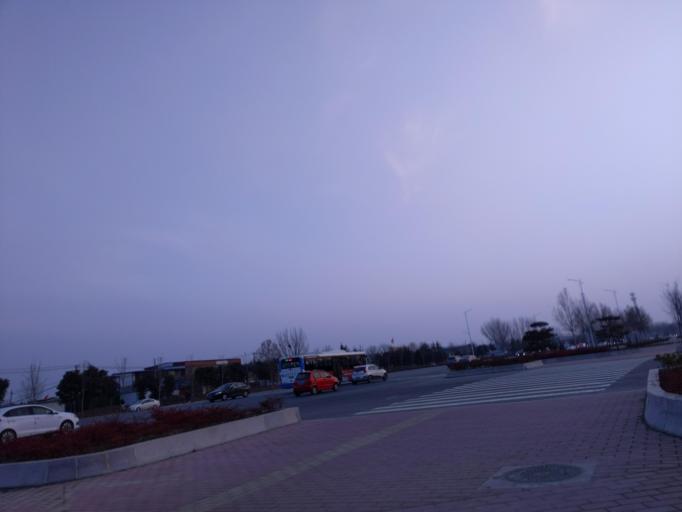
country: CN
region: Henan Sheng
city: Zhongyuanlu
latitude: 35.8123
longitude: 115.0661
